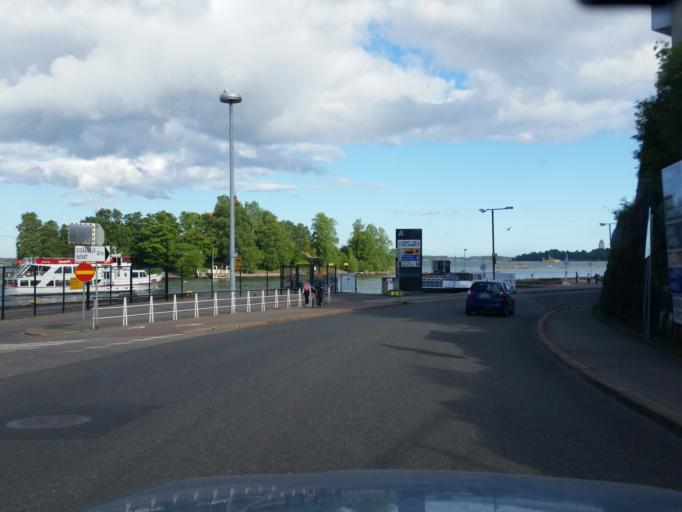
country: FI
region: Uusimaa
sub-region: Helsinki
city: Helsinki
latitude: 60.1601
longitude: 24.9599
